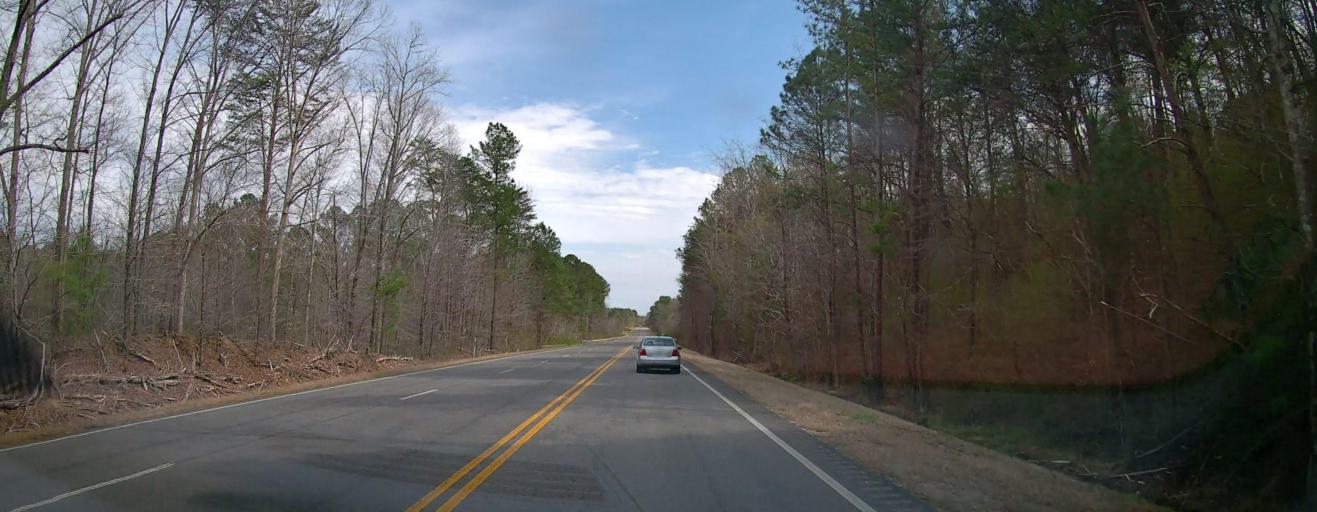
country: US
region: Alabama
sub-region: Walker County
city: Carbon Hill
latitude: 33.9115
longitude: -87.5602
